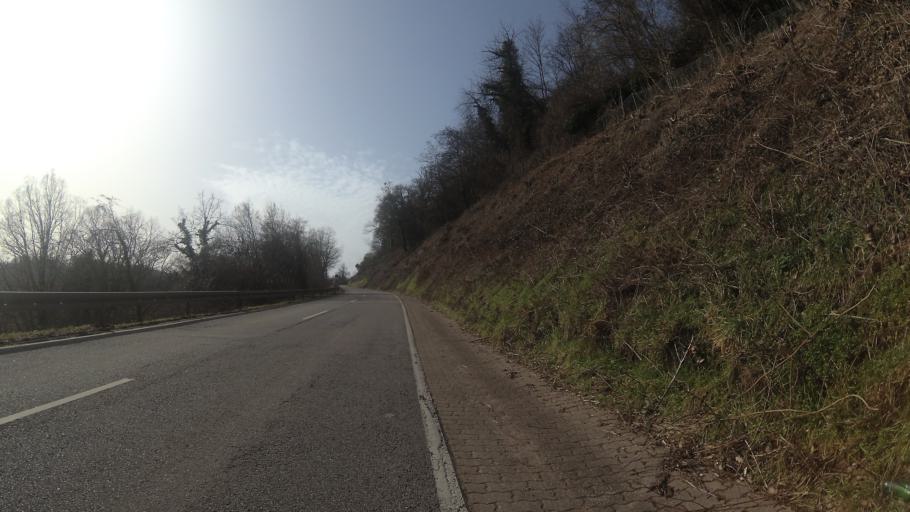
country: DE
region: Saarland
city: Uberherrn
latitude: 49.2677
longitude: 6.7037
